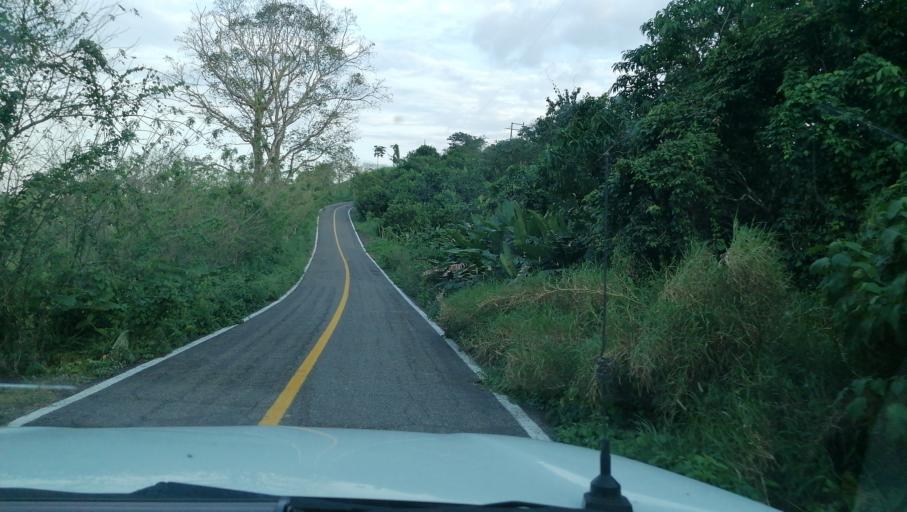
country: MX
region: Chiapas
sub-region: Juarez
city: El Triunfo 1ra. Seccion (Cardona)
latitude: 17.5067
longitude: -93.2288
